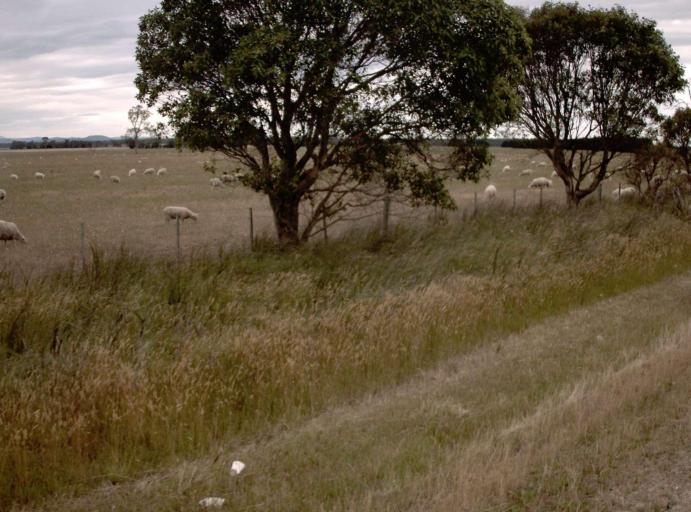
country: AU
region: Victoria
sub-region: East Gippsland
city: Bairnsdale
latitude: -37.9565
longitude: 147.5038
